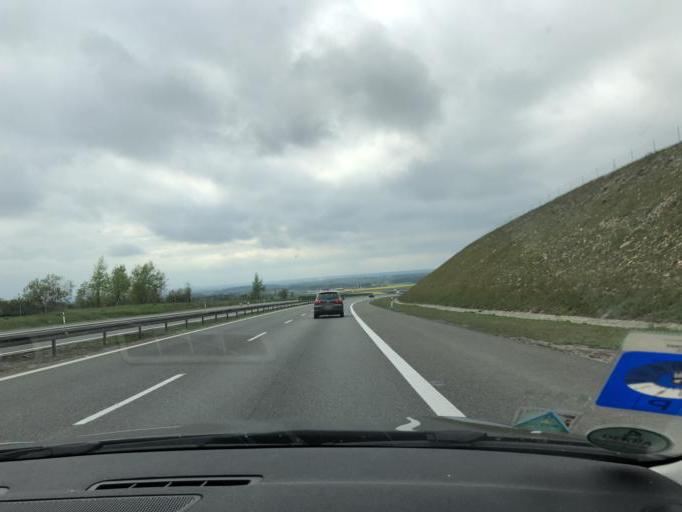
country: PL
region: Opole Voivodeship
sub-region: Powiat krapkowicki
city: Rozwadza
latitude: 50.4801
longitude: 18.1260
